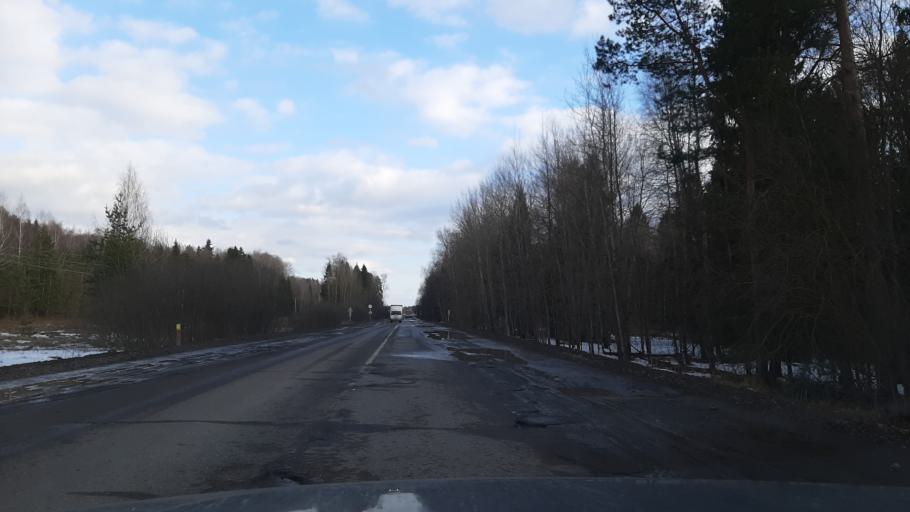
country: RU
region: Ivanovo
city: Novo-Talitsy
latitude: 56.9381
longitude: 40.7229
